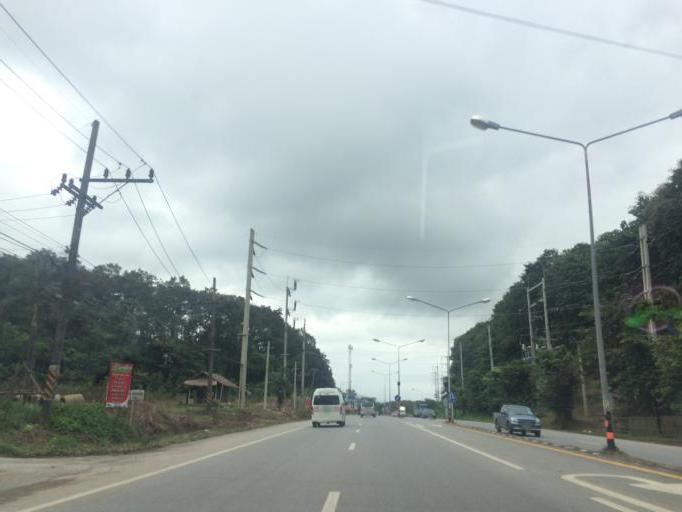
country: TH
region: Chiang Rai
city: Mae Chan
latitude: 20.1201
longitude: 99.8689
